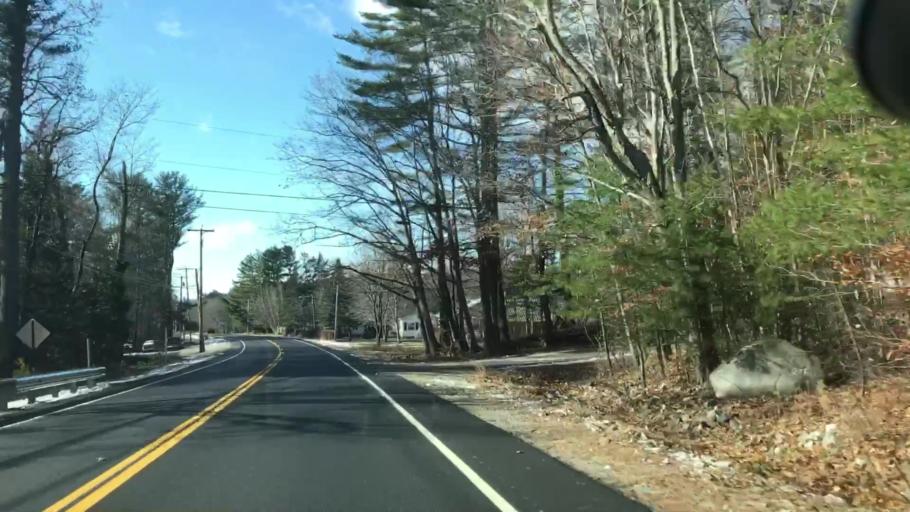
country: US
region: Maine
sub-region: Oxford County
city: Porter
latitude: 43.8048
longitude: -70.8966
